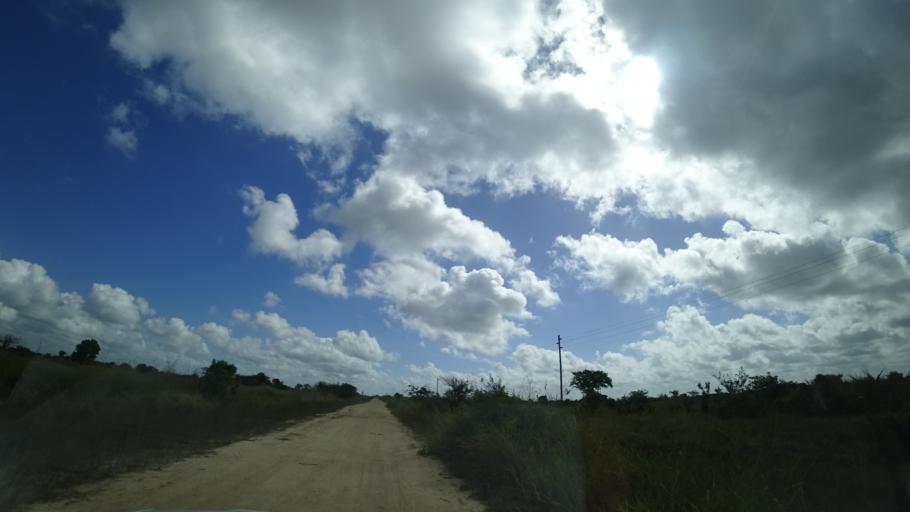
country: MZ
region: Sofala
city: Dondo
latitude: -19.4332
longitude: 34.5610
